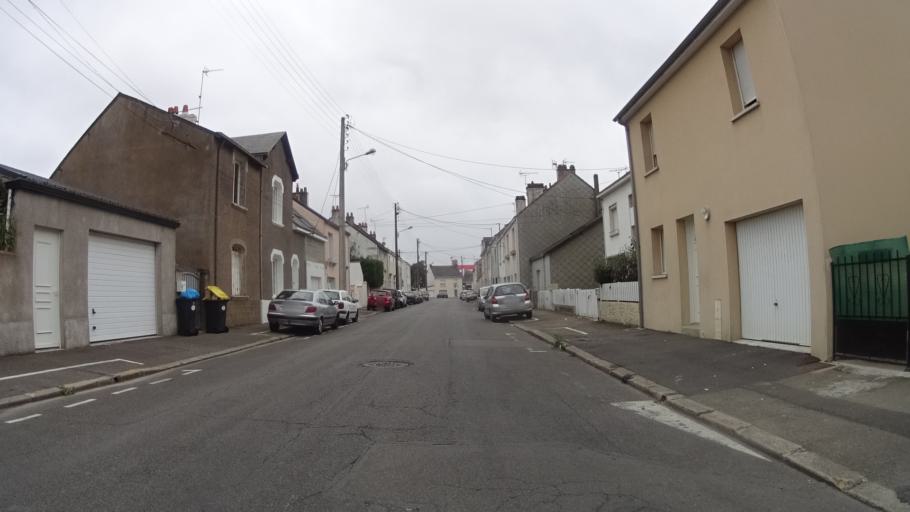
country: FR
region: Pays de la Loire
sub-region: Departement de la Loire-Atlantique
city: Trignac
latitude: 47.3002
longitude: -2.1928
